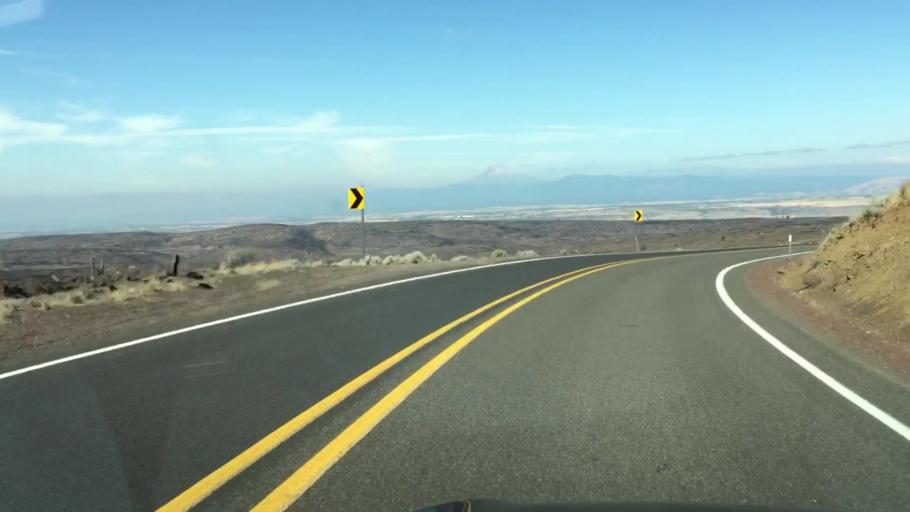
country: US
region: Oregon
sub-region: Jefferson County
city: Warm Springs
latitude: 45.1082
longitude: -121.0403
